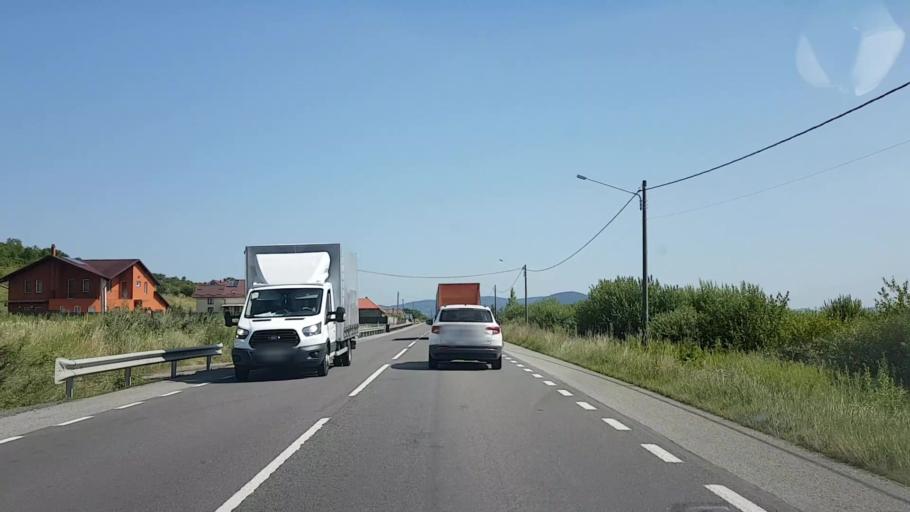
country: RO
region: Bistrita-Nasaud
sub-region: Comuna Sieu-Odorhei
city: Sieu-Odorhei
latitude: 47.1347
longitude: 24.3088
